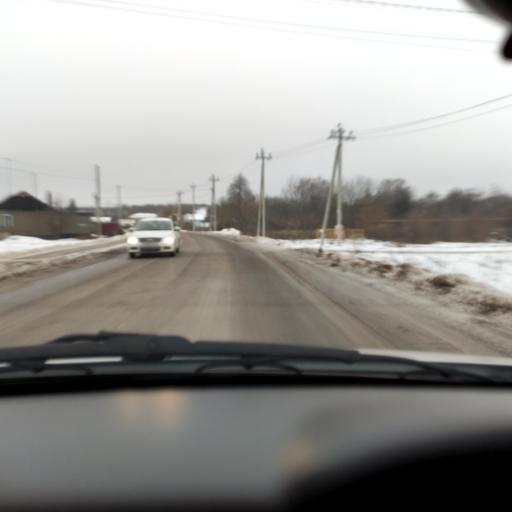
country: RU
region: Voronezj
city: Ramon'
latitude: 51.9095
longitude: 39.2859
